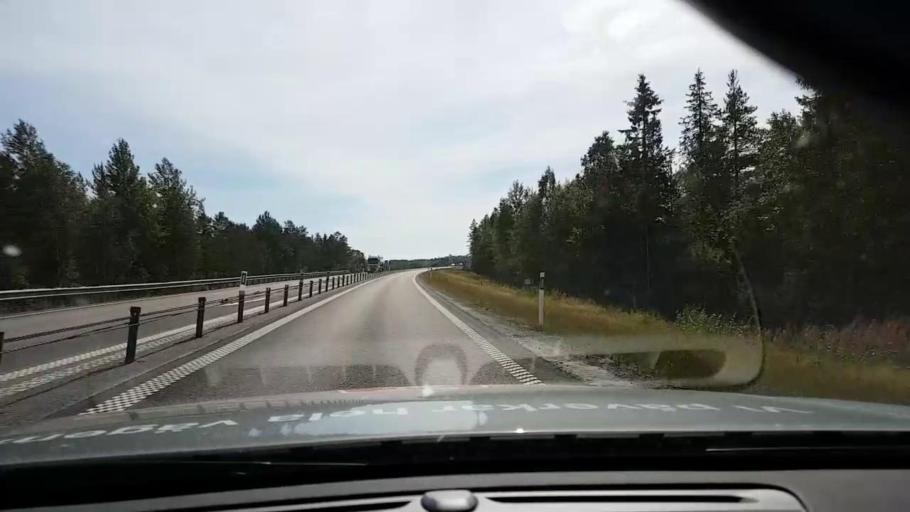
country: SE
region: Vaesternorrland
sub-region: OErnskoeldsviks Kommun
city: Husum
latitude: 63.3725
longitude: 19.1896
